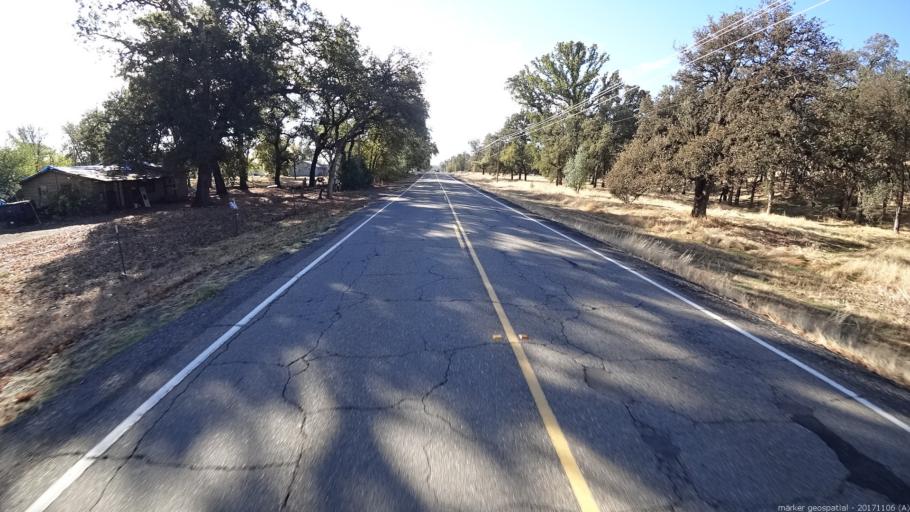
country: US
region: California
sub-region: Shasta County
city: Palo Cedro
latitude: 40.5162
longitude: -122.2385
